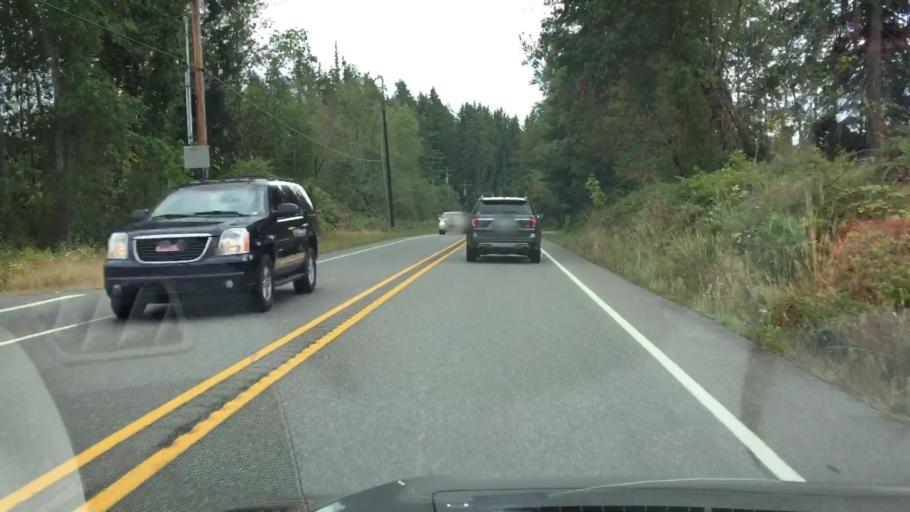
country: US
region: Washington
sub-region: Pierce County
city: Eatonville
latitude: 46.9298
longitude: -122.2816
